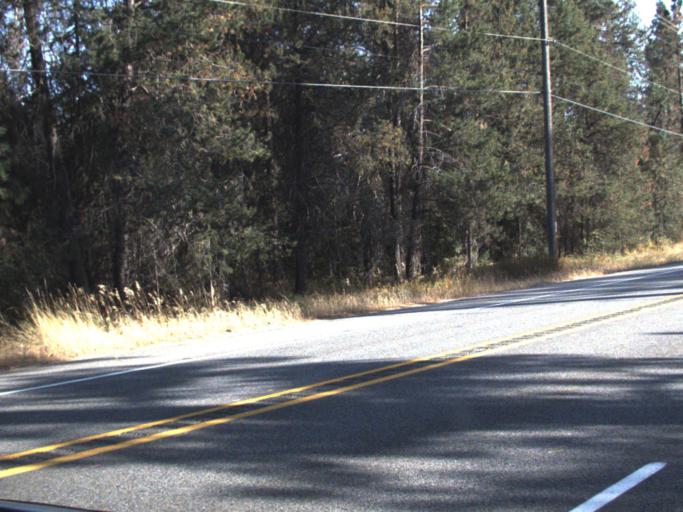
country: US
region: Washington
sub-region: Spokane County
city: Deer Park
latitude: 47.9923
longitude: -117.3496
